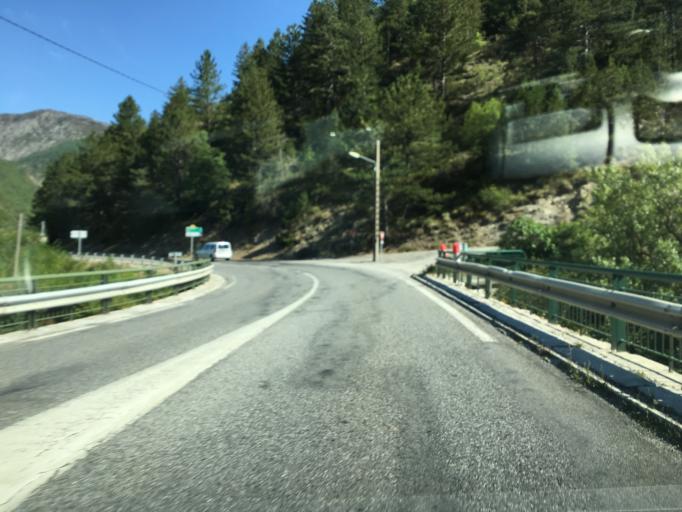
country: FR
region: Provence-Alpes-Cote d'Azur
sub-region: Departement des Hautes-Alpes
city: Serres
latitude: 44.4322
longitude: 5.7133
